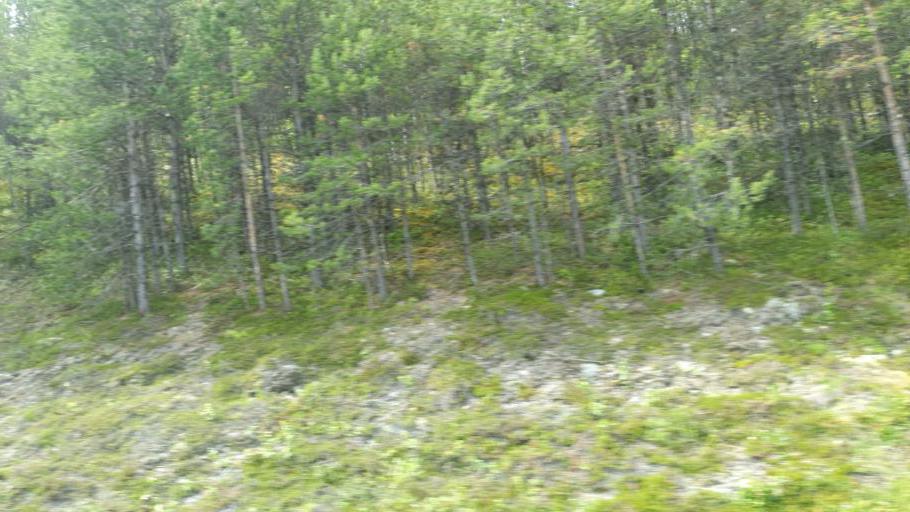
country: NO
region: Oppland
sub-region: Vaga
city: Vagamo
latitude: 61.7116
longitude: 9.0543
